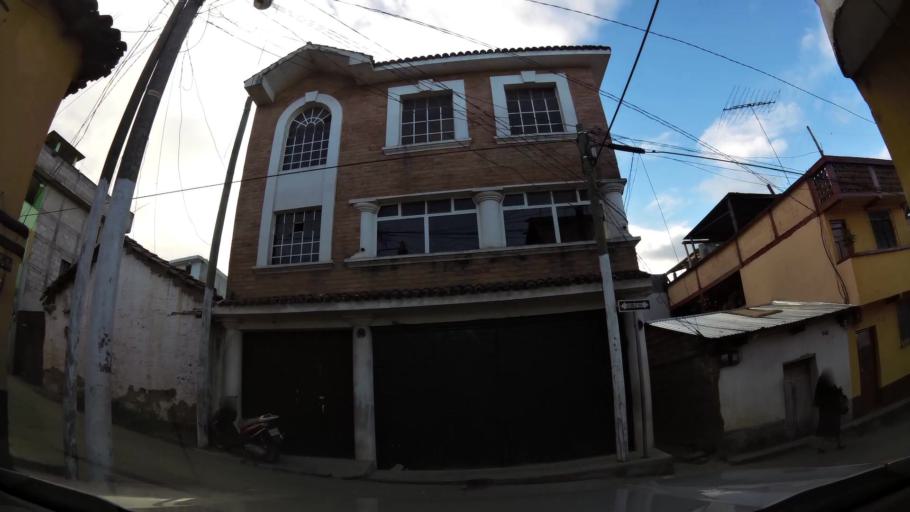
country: GT
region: Quiche
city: Chichicastenango
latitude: 14.9408
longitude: -91.1128
